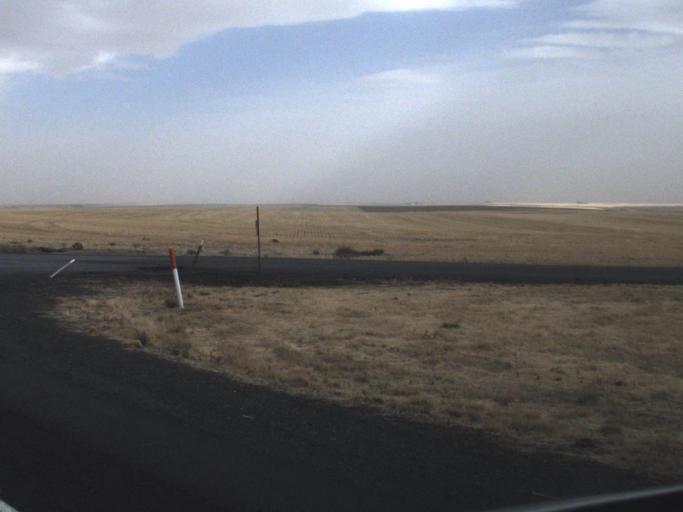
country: US
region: Washington
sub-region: Adams County
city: Ritzville
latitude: 47.4224
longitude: -118.3575
